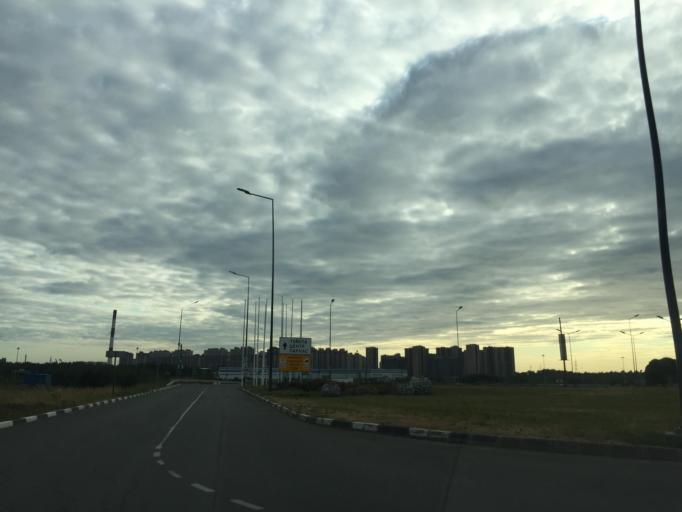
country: RU
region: Leningrad
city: Bugry
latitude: 60.0887
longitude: 30.3815
